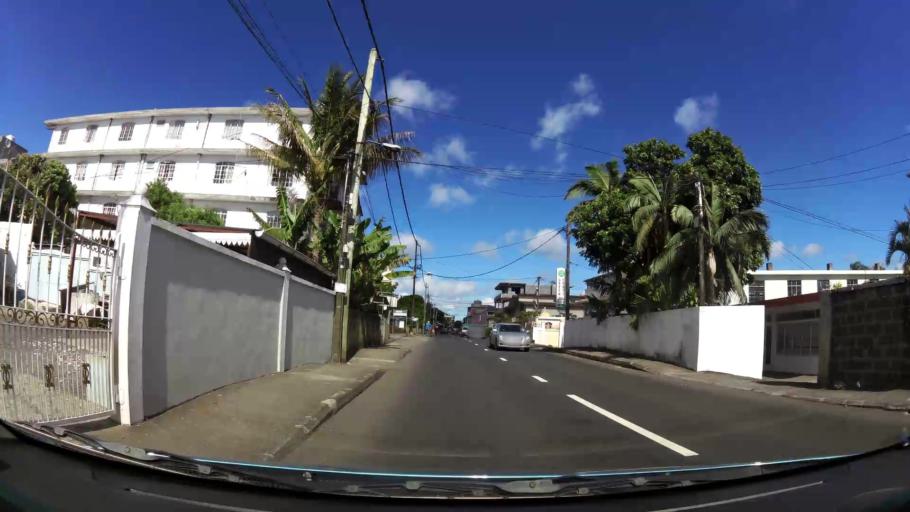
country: MU
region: Plaines Wilhems
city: Vacoas
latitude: -20.3068
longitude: 57.4914
